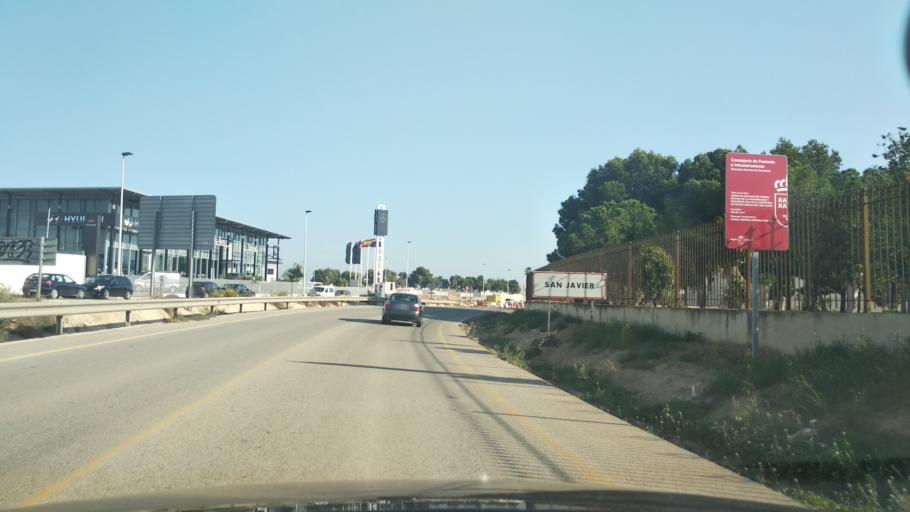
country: ES
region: Murcia
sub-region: Murcia
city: San Javier
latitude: 37.8133
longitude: -0.8401
